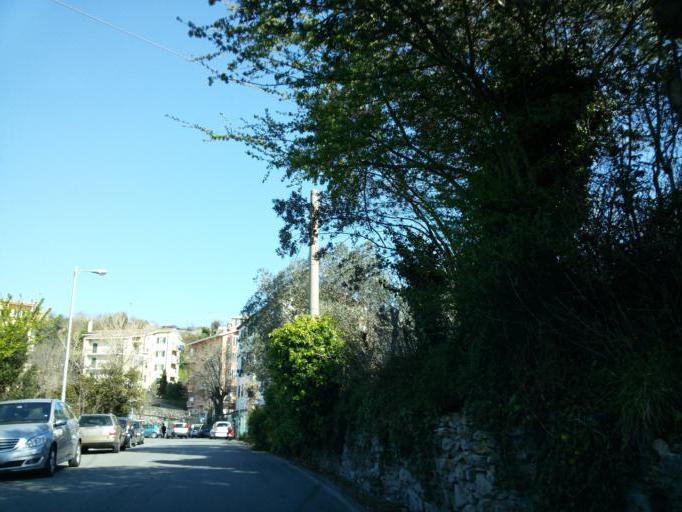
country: IT
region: Liguria
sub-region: Provincia di Genova
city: Genoa
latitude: 44.4277
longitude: 8.9087
